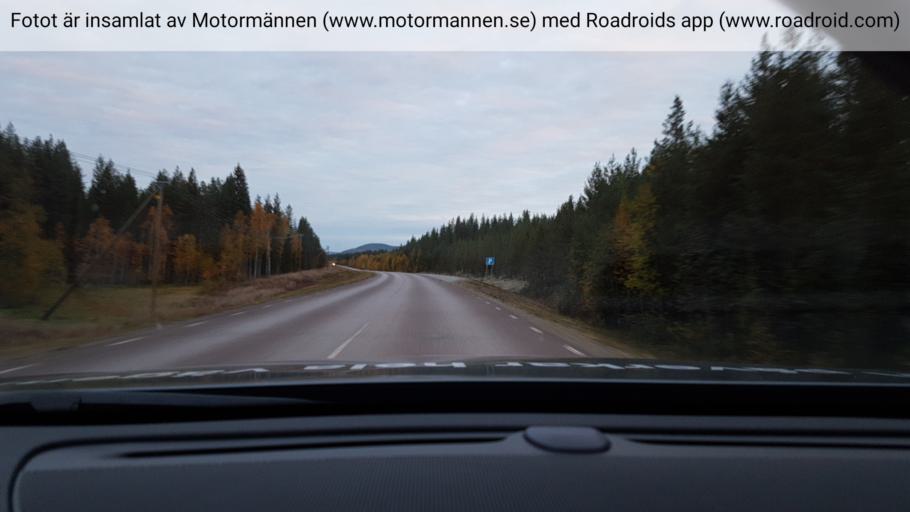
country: SE
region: Norrbotten
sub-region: Alvsbyns Kommun
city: AElvsbyn
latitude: 65.8799
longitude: 20.3607
